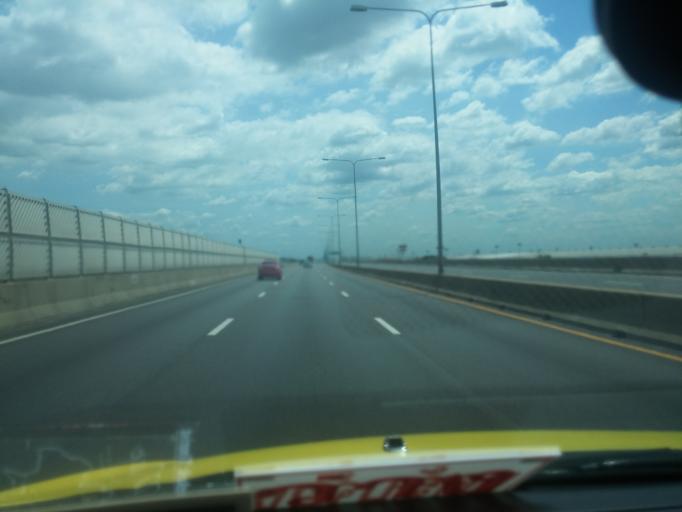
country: TH
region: Bangkok
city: Don Mueang
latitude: 13.9036
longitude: 100.5923
